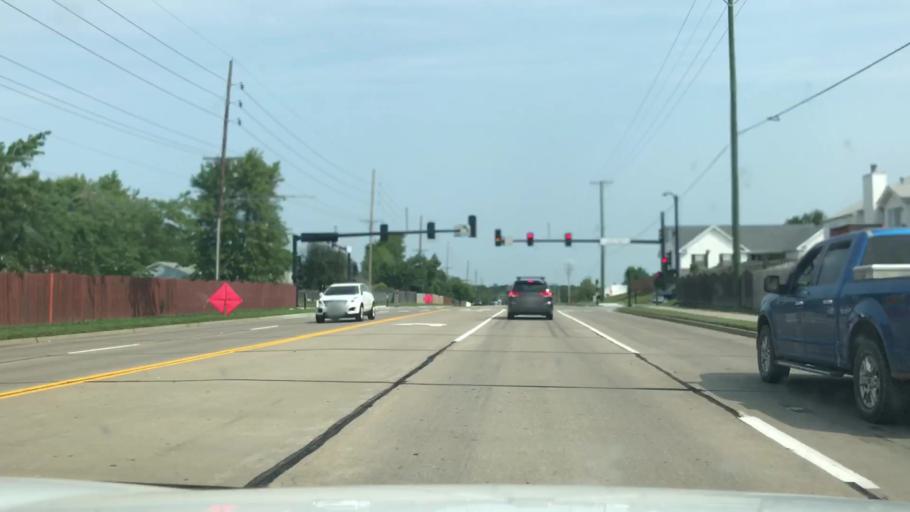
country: US
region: Missouri
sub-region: Saint Charles County
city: Dardenne Prairie
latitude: 38.7840
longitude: -90.7371
